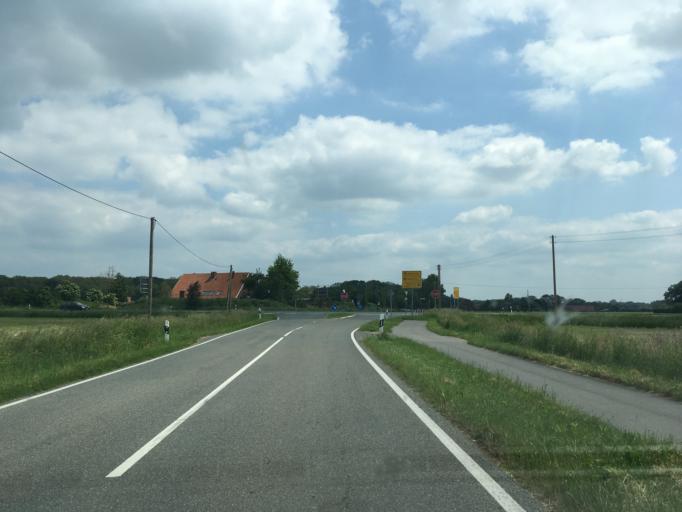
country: DE
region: North Rhine-Westphalia
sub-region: Regierungsbezirk Munster
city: Raesfeld
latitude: 51.7867
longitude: 6.7708
